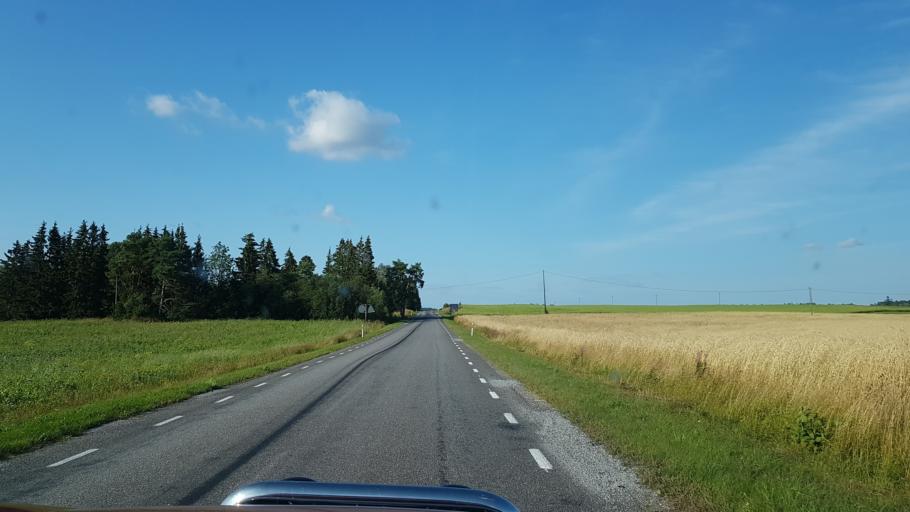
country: EE
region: Jaervamaa
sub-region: Jaerva-Jaani vald
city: Jarva-Jaani
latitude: 59.1217
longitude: 25.6597
